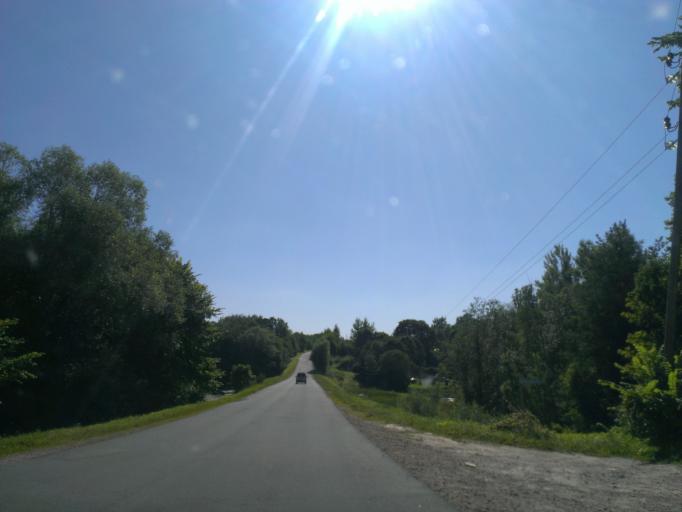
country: LV
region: Sigulda
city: Sigulda
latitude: 57.1314
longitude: 24.8371
